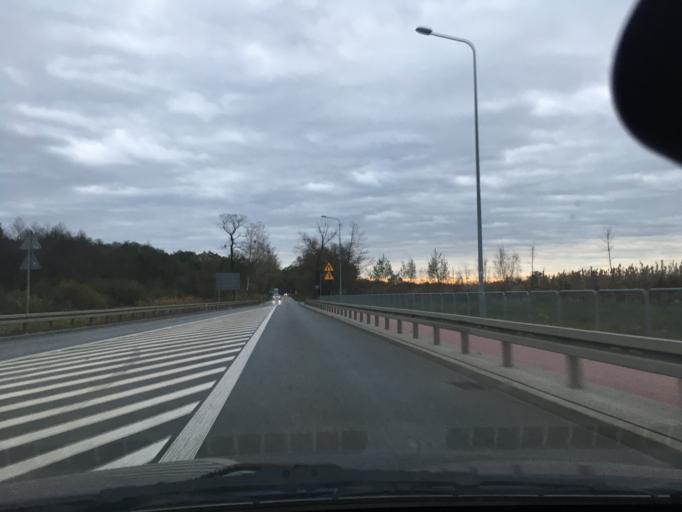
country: PL
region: Masovian Voivodeship
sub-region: Powiat pruszkowski
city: Nadarzyn
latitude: 52.1034
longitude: 20.8397
